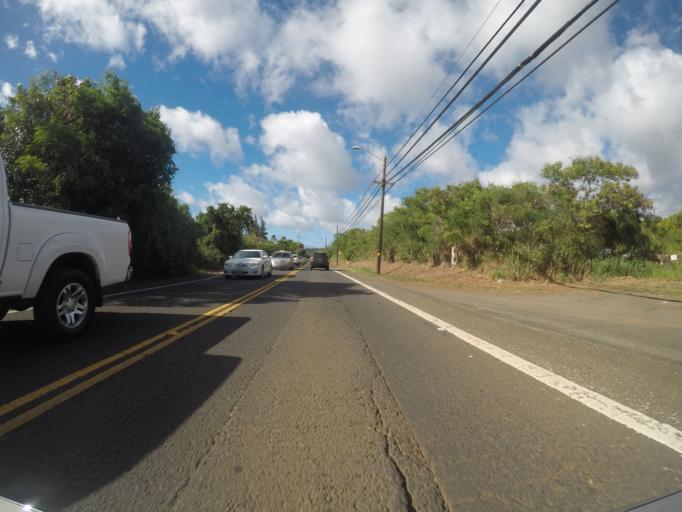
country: US
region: Hawaii
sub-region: Honolulu County
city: Pupukea
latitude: 21.6271
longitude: -158.0742
